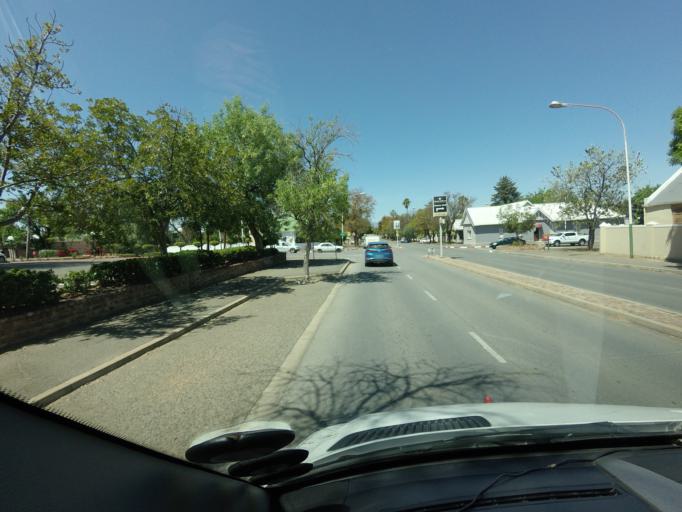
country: ZA
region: Western Cape
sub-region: Eden District Municipality
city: Oudtshoorn
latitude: -33.5840
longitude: 22.2043
